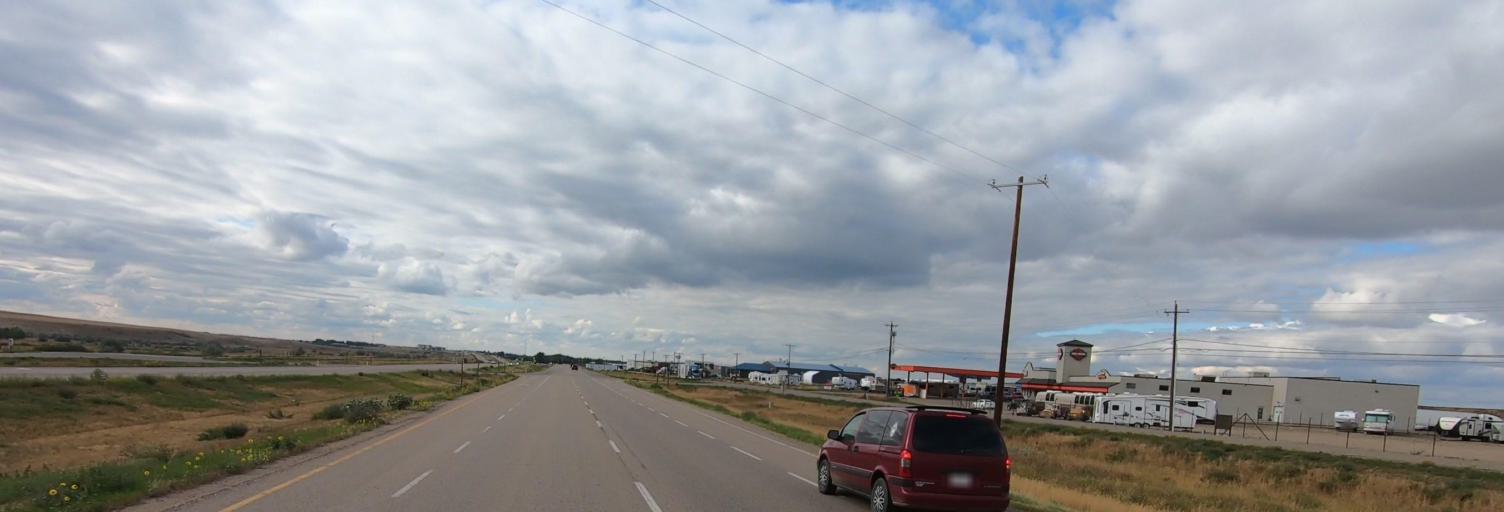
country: CA
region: Alberta
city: Medicine Hat
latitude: 49.9726
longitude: -110.6047
